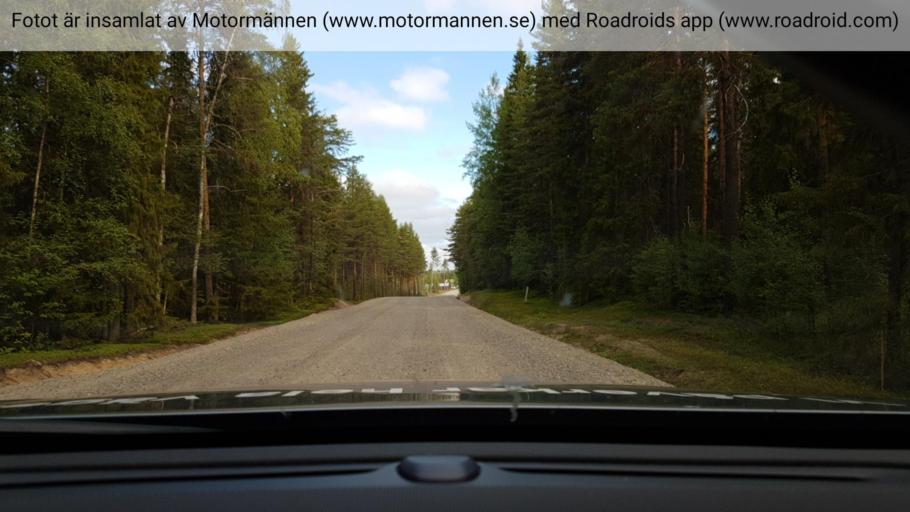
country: SE
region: Vaesterbotten
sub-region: Norsjo Kommun
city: Norsjoe
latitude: 64.6474
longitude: 19.2811
